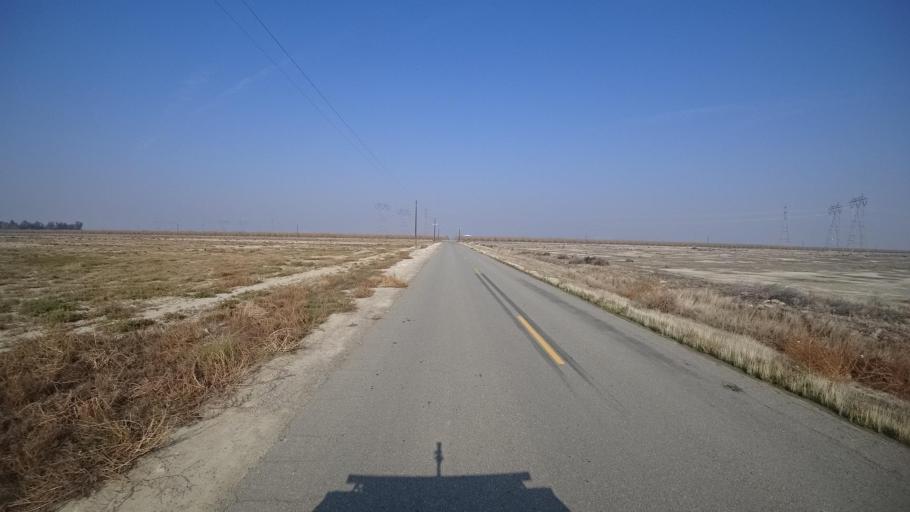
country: US
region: California
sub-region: Kern County
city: Buttonwillow
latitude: 35.3523
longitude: -119.3591
